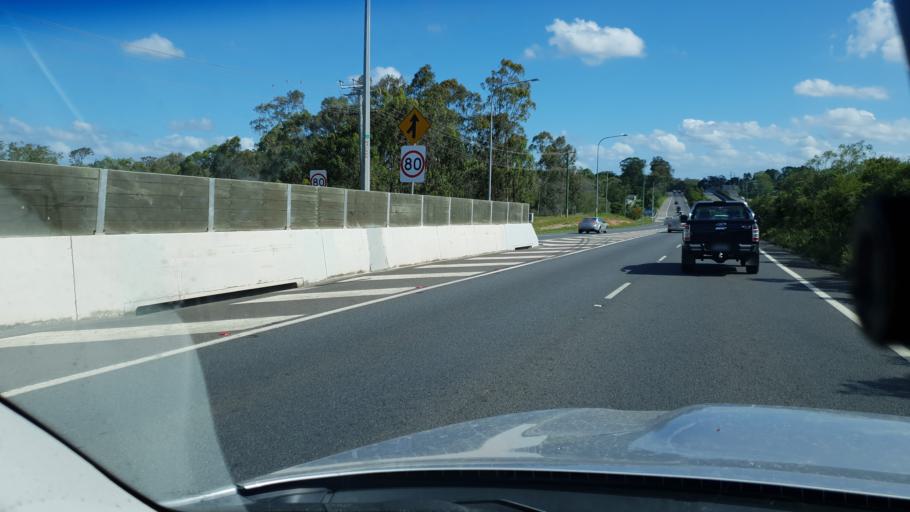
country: AU
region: Queensland
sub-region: Logan
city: Park Ridge South
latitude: -27.6793
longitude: 153.0312
